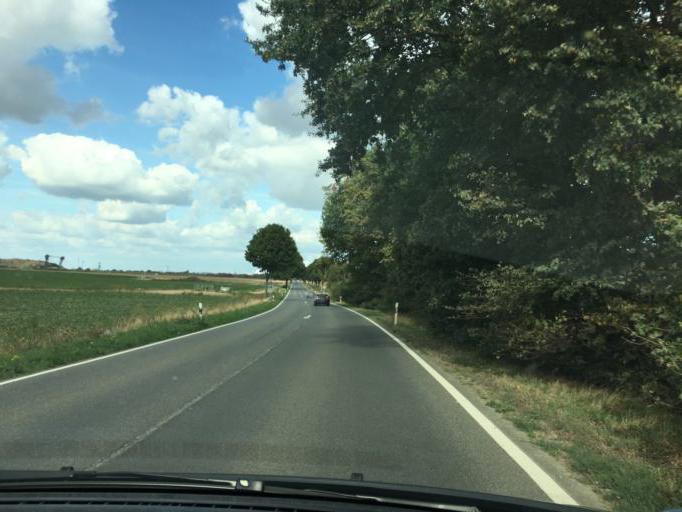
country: DE
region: North Rhine-Westphalia
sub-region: Regierungsbezirk Koln
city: Elsdorf
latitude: 50.8955
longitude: 6.6117
